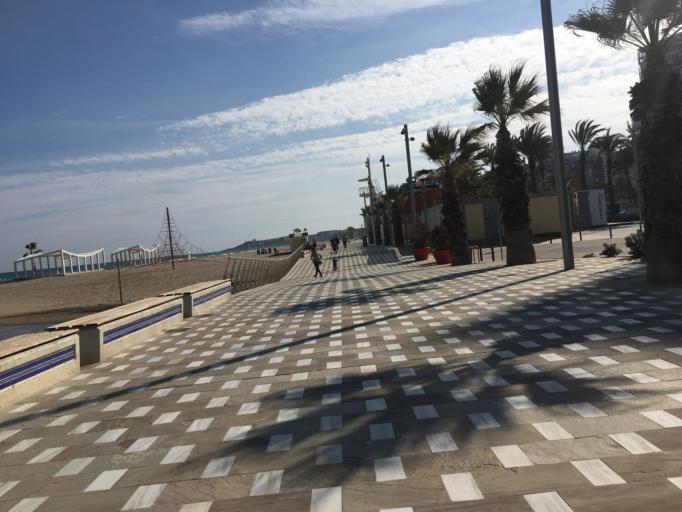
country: ES
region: Valencia
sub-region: Provincia de Alicante
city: San Juan de Alicante
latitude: 38.3754
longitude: -0.4101
